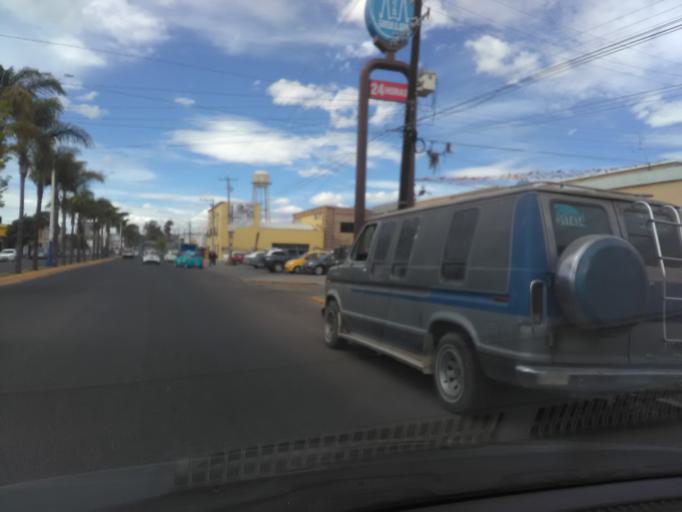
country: MX
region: Durango
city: Victoria de Durango
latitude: 24.0386
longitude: -104.6720
